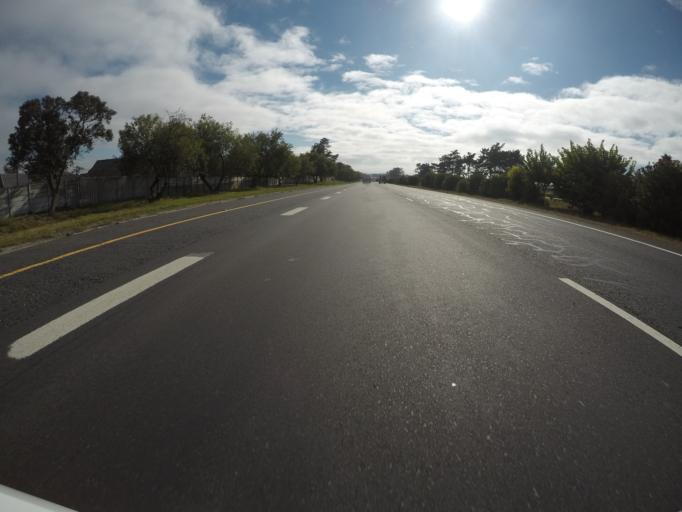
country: ZA
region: Western Cape
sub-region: City of Cape Town
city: Kraaifontein
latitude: -33.8544
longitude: 18.7007
